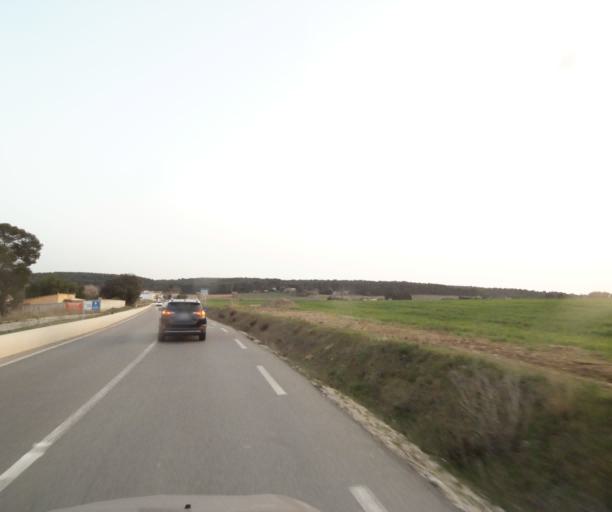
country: FR
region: Provence-Alpes-Cote d'Azur
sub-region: Departement des Bouches-du-Rhone
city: Cabries
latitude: 43.4444
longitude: 5.3606
